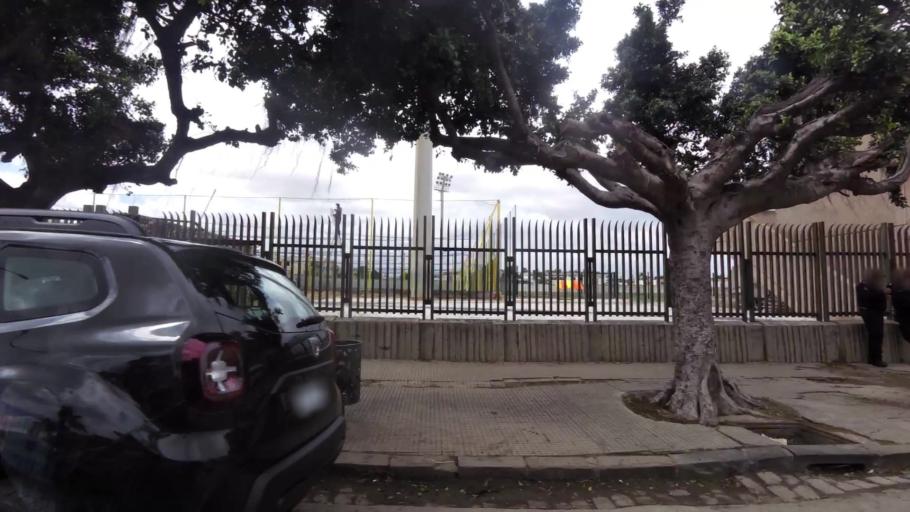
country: MA
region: Grand Casablanca
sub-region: Casablanca
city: Casablanca
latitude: 33.5816
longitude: -7.6483
